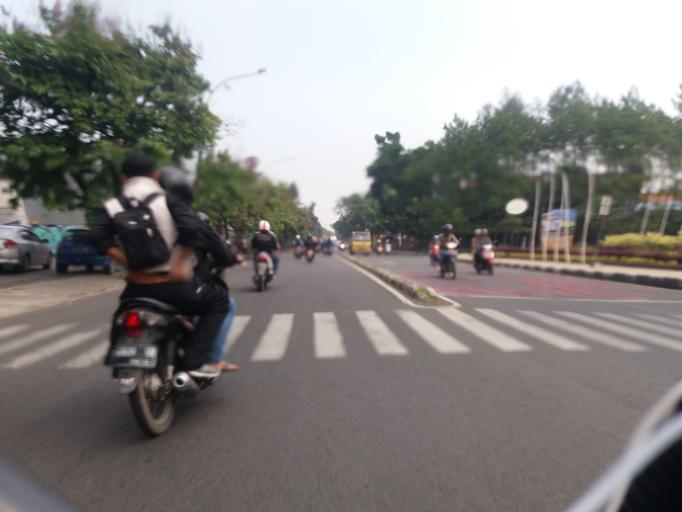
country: ID
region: West Java
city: Bandung
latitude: -6.9069
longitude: 107.5876
